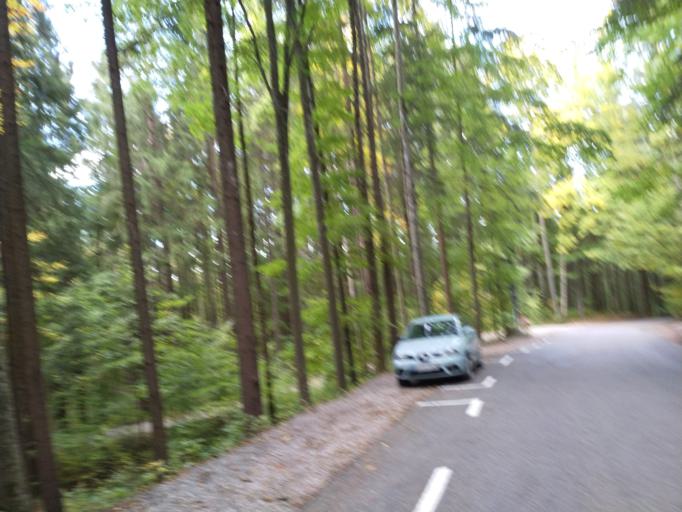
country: AT
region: Tyrol
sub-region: Politischer Bezirk Reutte
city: Vils
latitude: 47.5645
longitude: 10.6402
